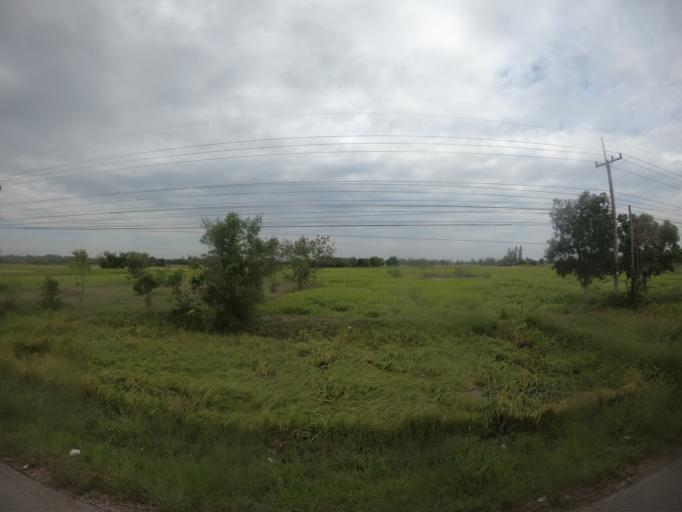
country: TH
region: Maha Sarakham
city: Kantharawichai
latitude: 16.3294
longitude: 103.2643
